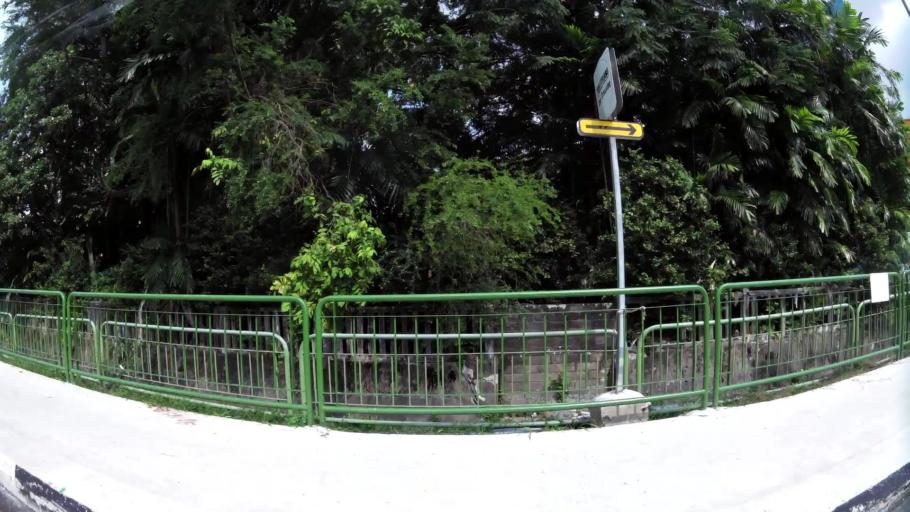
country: SG
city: Singapore
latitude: 1.3064
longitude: 103.9128
